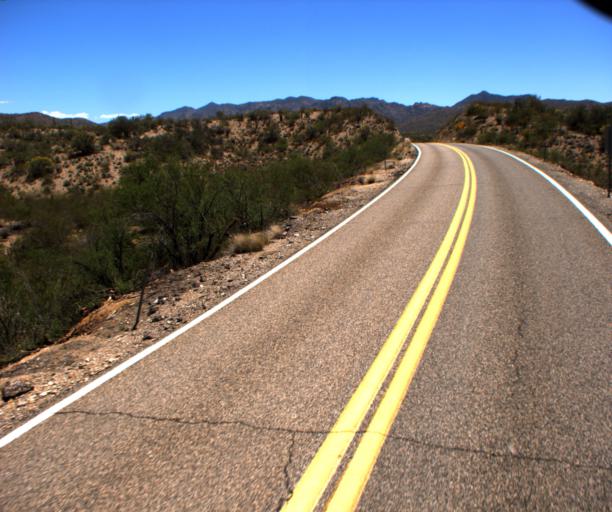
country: US
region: Arizona
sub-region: Yavapai County
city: Bagdad
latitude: 34.4843
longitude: -113.0640
